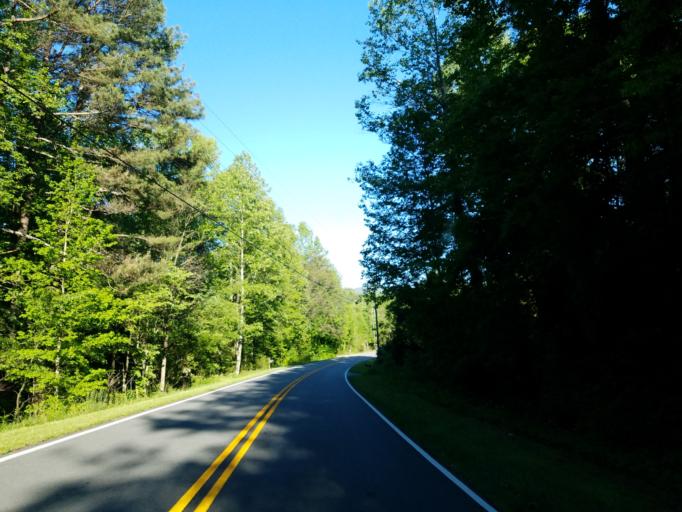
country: US
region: Georgia
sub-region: Fannin County
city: Blue Ridge
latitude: 34.6914
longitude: -84.3076
